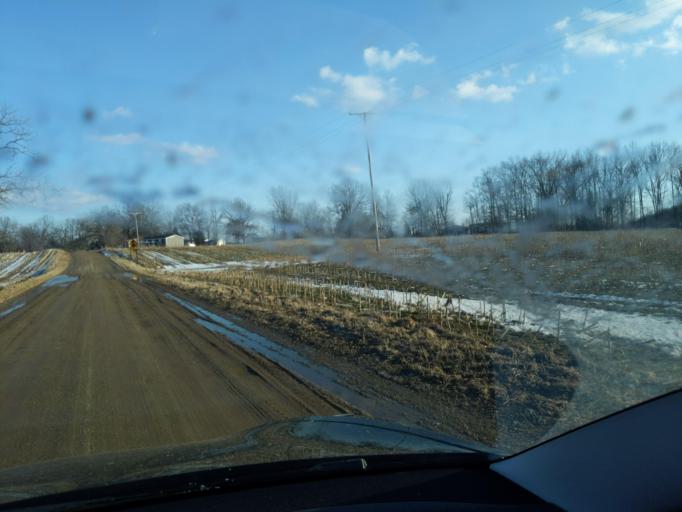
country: US
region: Michigan
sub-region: Ingham County
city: Stockbridge
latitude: 42.5199
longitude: -84.1844
